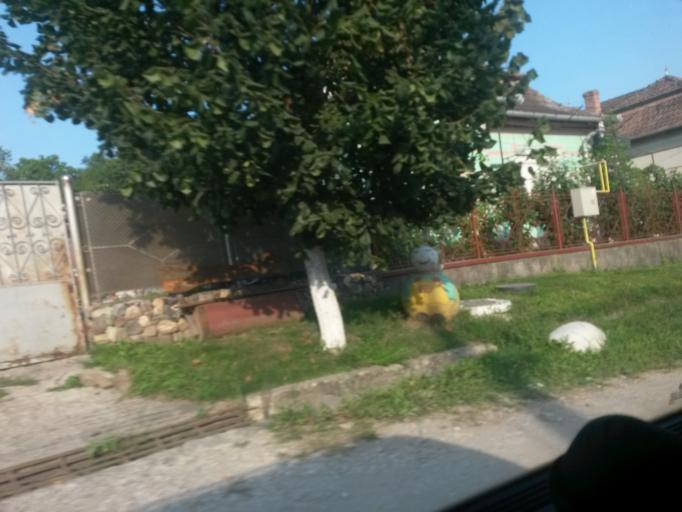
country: RO
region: Alba
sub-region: Municipiul Aiud
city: Aiudul de Sus
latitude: 46.3234
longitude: 23.6827
